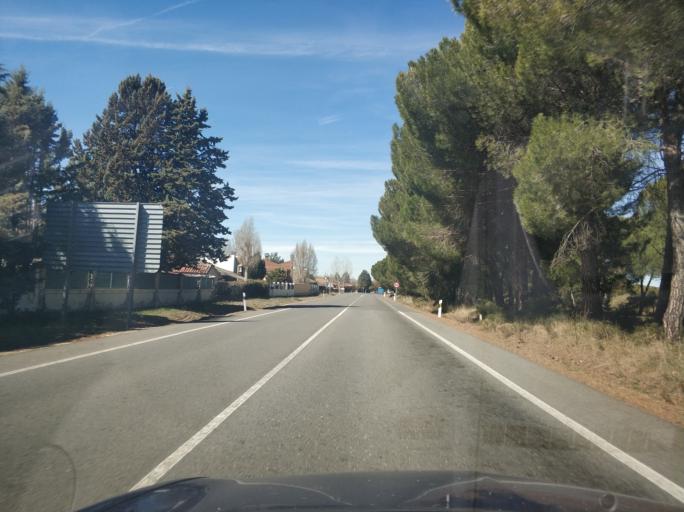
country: ES
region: Castille and Leon
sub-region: Provincia de Valladolid
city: Viana de Cega
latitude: 41.5428
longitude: -4.7785
